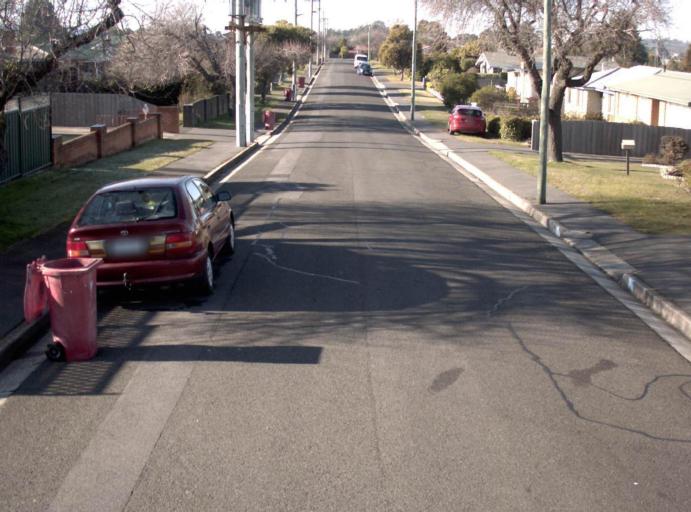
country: AU
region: Tasmania
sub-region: Launceston
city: Summerhill
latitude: -41.4672
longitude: 147.1208
